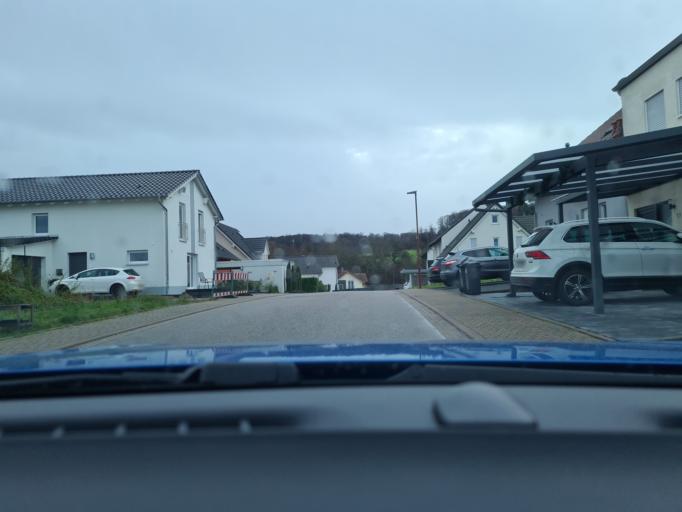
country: DE
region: Baden-Wuerttemberg
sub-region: Karlsruhe Region
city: Dielheim
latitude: 49.2834
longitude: 8.7257
